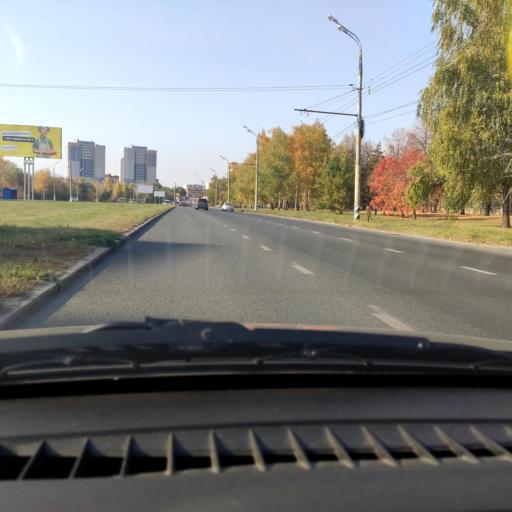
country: RU
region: Samara
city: Tol'yatti
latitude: 53.5032
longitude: 49.2603
